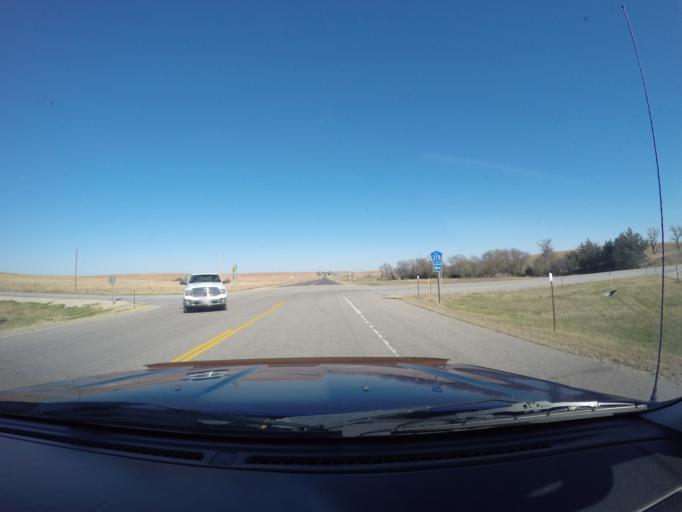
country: US
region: Kansas
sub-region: Marshall County
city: Blue Rapids
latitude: 39.4359
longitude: -96.7643
